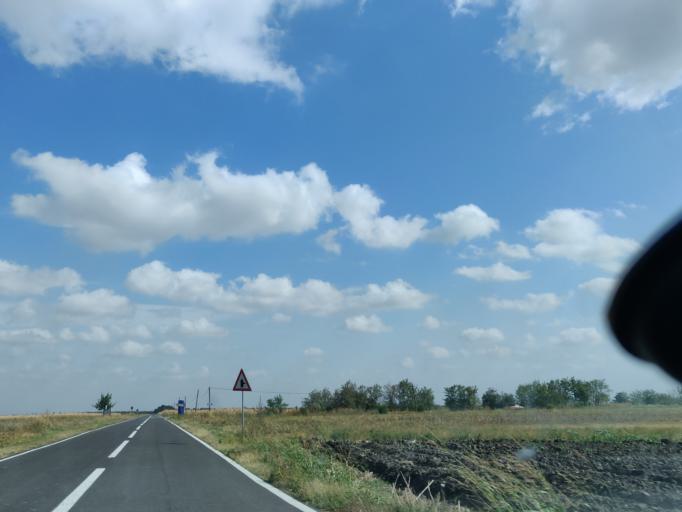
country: RO
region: Vrancea
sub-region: Comuna Maicanesti
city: Ramniceni
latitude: 45.4693
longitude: 27.4254
